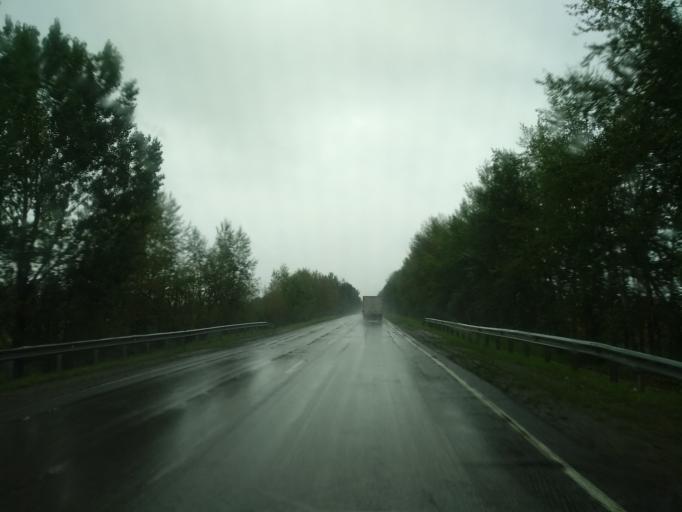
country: RU
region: Voronezj
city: Verkhnyaya Khava
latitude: 51.6847
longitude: 39.9128
